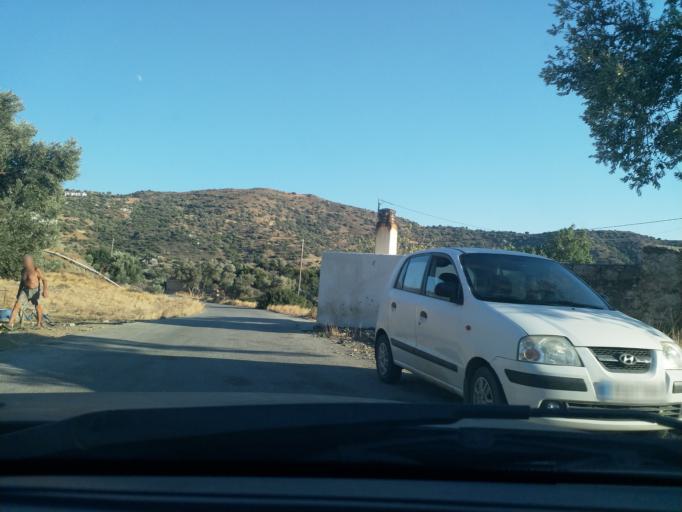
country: GR
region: Crete
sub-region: Nomos Rethymnis
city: Agia Galini
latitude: 35.1173
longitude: 24.5626
